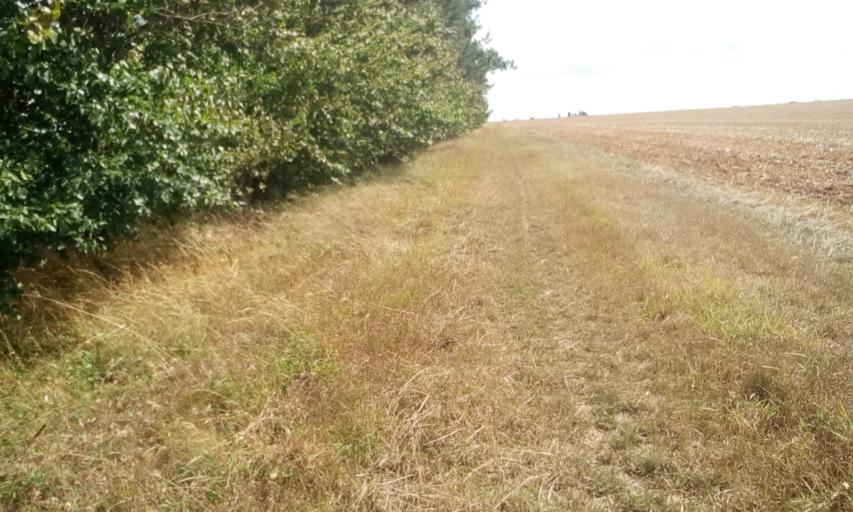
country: FR
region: Lower Normandy
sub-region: Departement du Calvados
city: Saint-Sylvain
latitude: 49.0798
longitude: -0.1982
